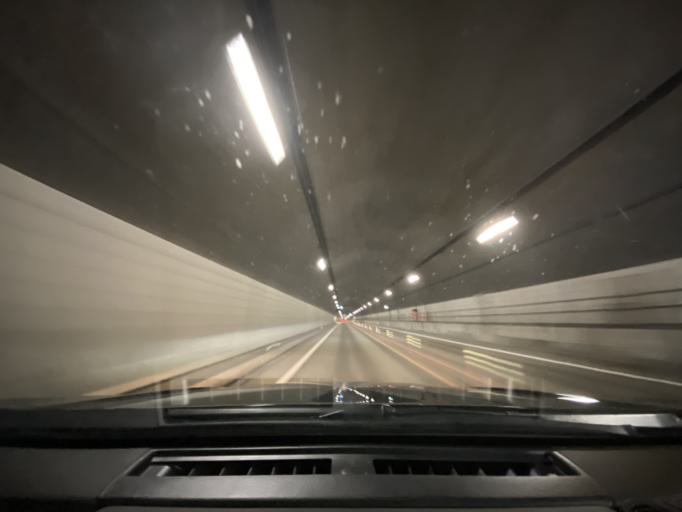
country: JP
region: Hokkaido
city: Shimo-furano
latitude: 43.0366
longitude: 142.4664
